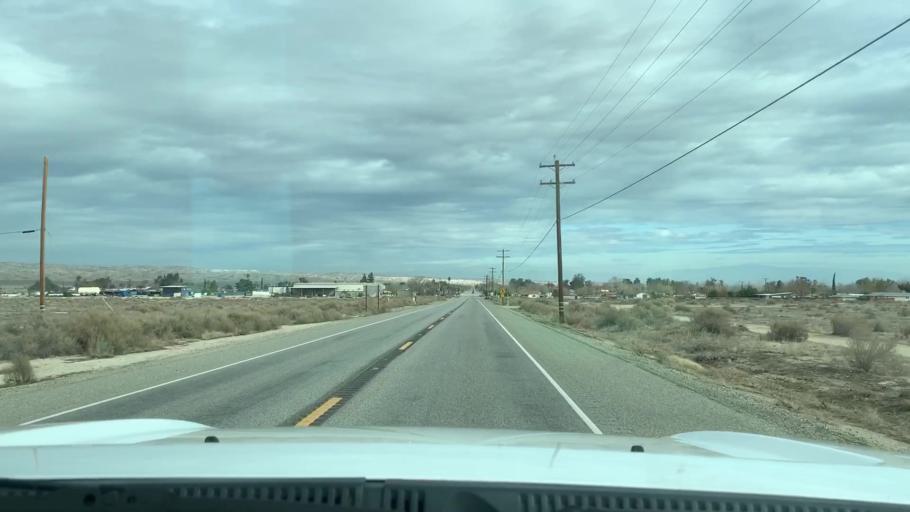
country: US
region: California
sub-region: Kern County
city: Ford City
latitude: 35.2030
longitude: -119.4149
